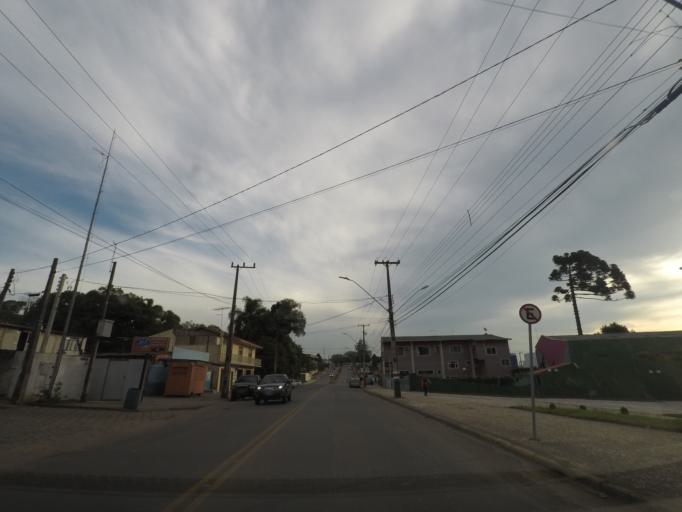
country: BR
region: Parana
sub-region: Colombo
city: Colombo
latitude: -25.2903
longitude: -49.2198
